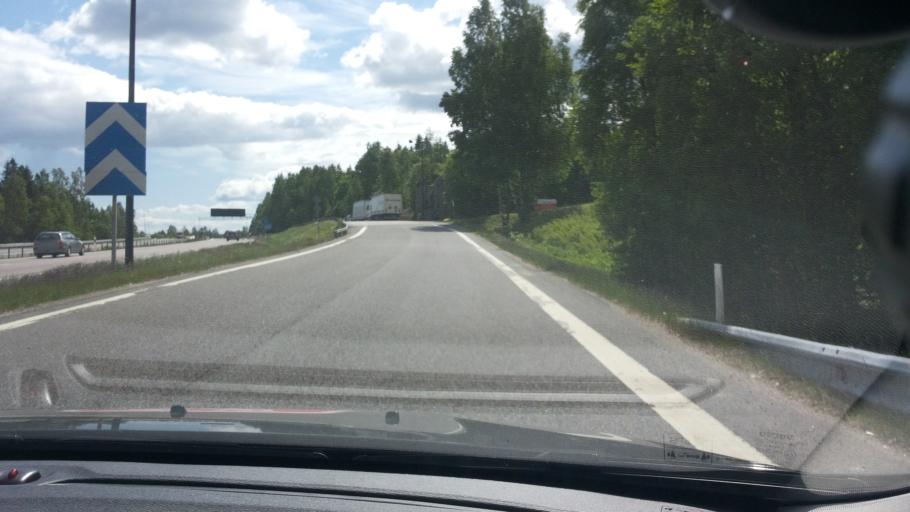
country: SE
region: Vaesternorrland
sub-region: Sundsvalls Kommun
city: Sundsbruk
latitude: 62.4618
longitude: 17.3386
